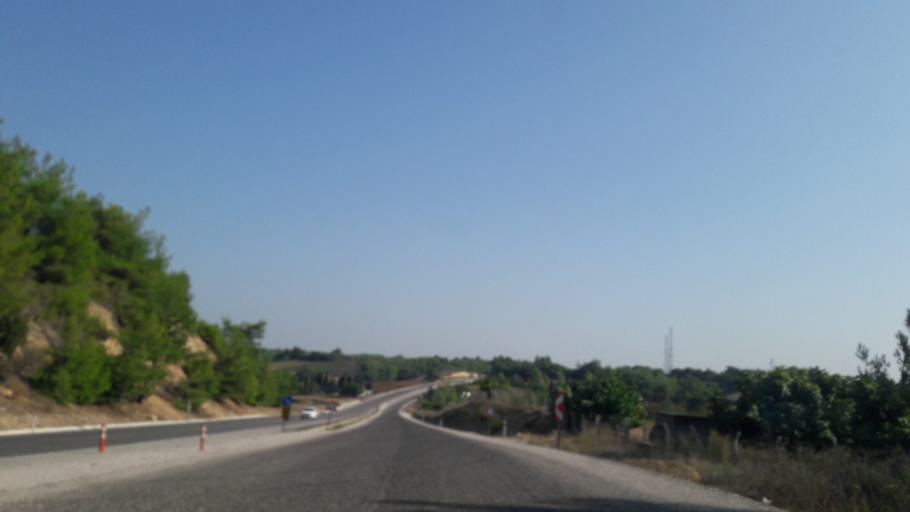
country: TR
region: Adana
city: Sagkaya
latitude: 37.1736
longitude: 35.5645
